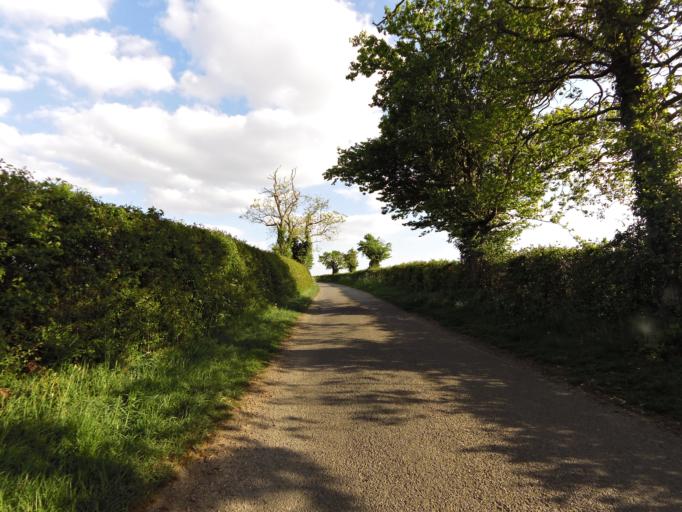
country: GB
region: England
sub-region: Suffolk
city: Halesworth
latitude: 52.4025
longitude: 1.5081
